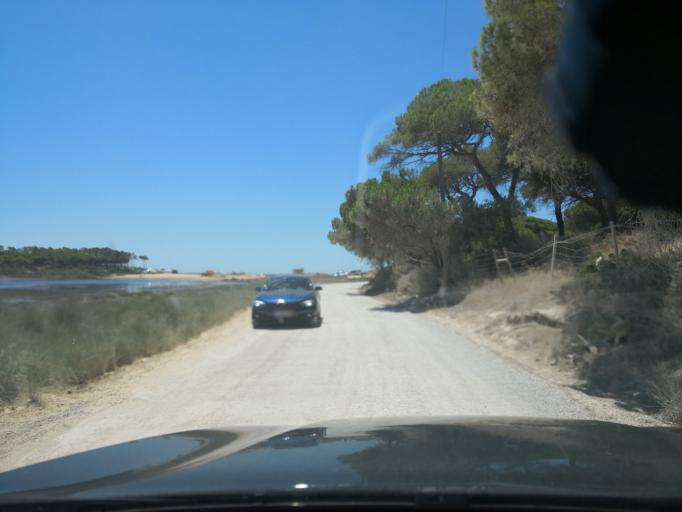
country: PT
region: Faro
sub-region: Loule
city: Quarteira
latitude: 37.0611
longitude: -8.0840
